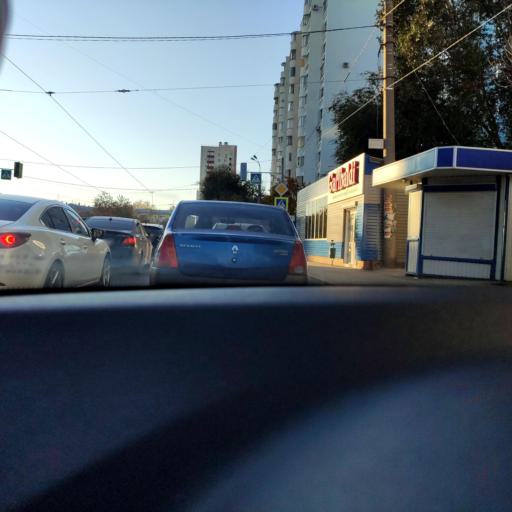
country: RU
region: Samara
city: Samara
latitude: 53.1892
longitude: 50.1380
